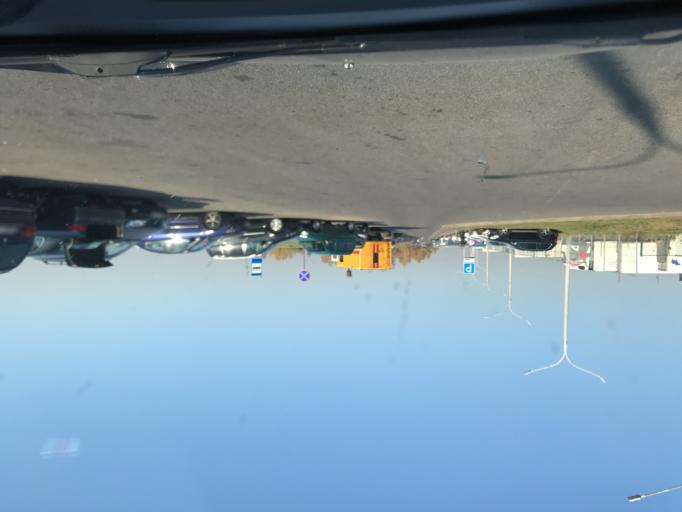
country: BY
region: Minsk
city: Pryvol'ny
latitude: 53.8139
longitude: 27.7871
